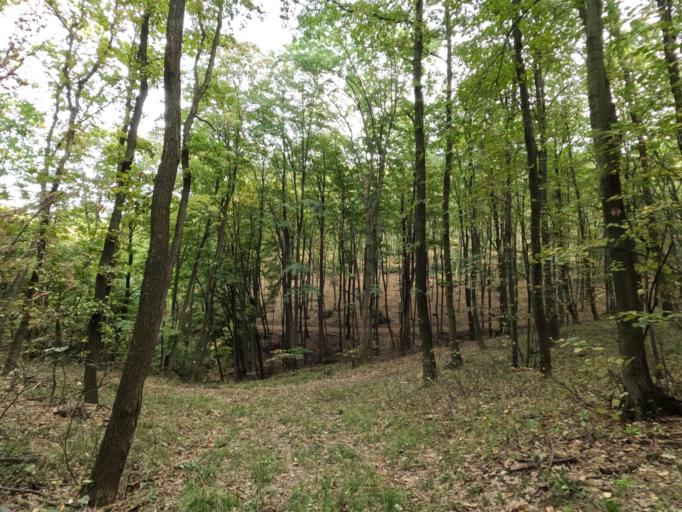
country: HU
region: Tolna
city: Szekszard
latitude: 46.3149
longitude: 18.6610
